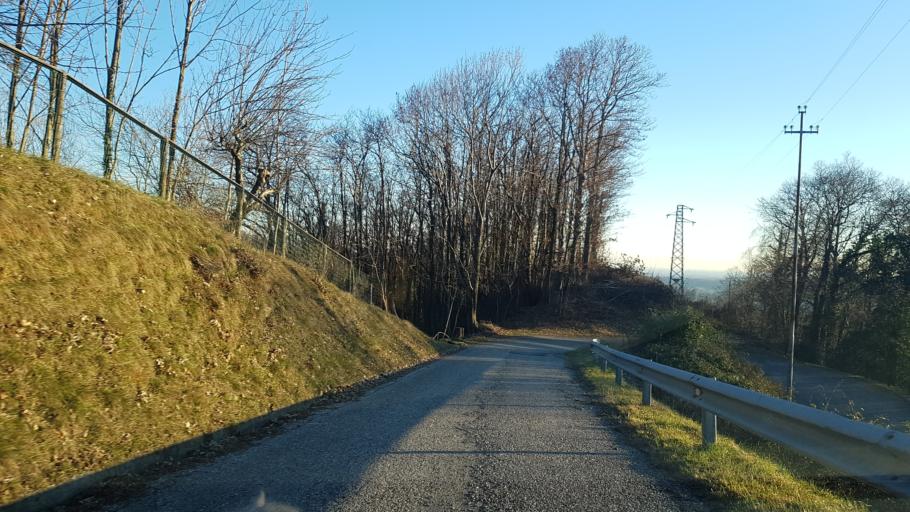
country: IT
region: Friuli Venezia Giulia
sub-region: Provincia di Udine
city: Tarcento
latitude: 46.2384
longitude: 13.2254
